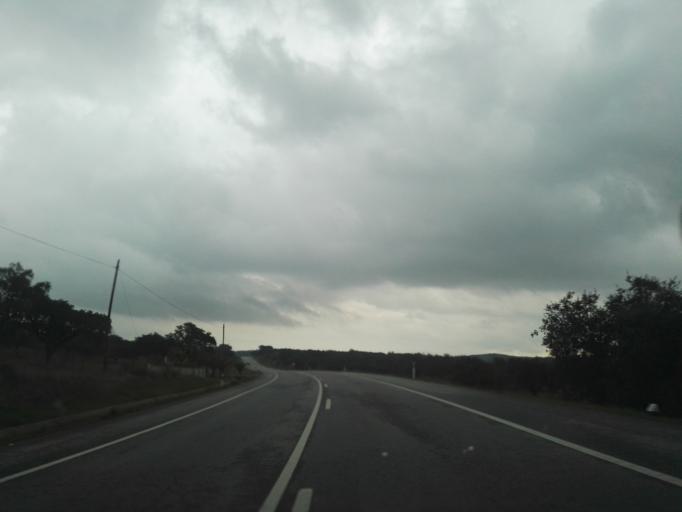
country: PT
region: Portalegre
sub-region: Portalegre
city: Urra
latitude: 39.1911
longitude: -7.3579
